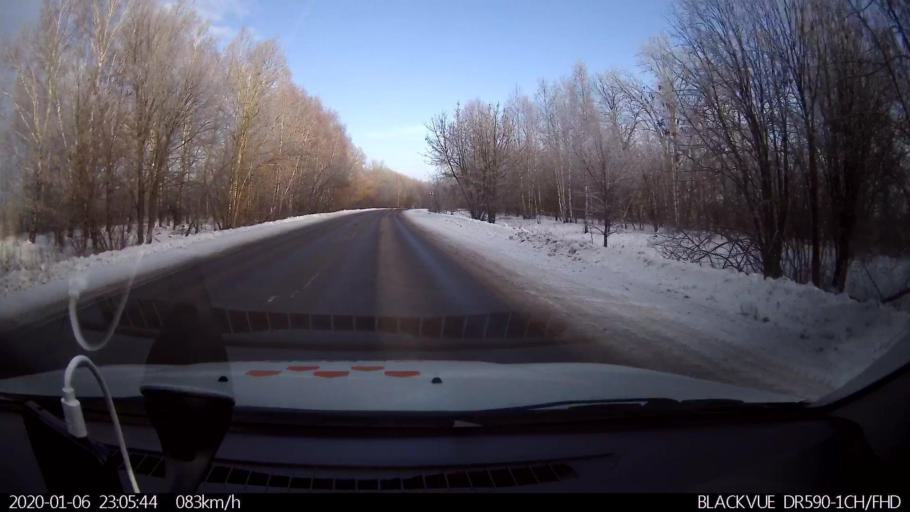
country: RU
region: Nizjnij Novgorod
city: Bogorodsk
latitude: 56.1227
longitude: 43.5606
